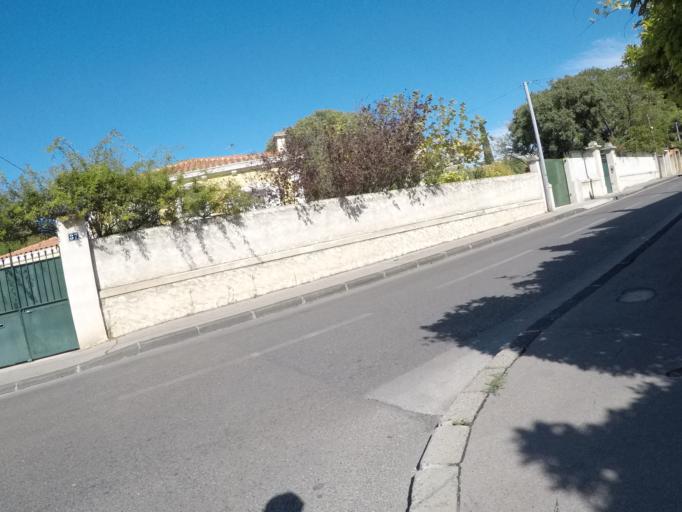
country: FR
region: Provence-Alpes-Cote d'Azur
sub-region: Departement des Bouches-du-Rhone
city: Marseille 09
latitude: 43.2459
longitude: 5.4078
